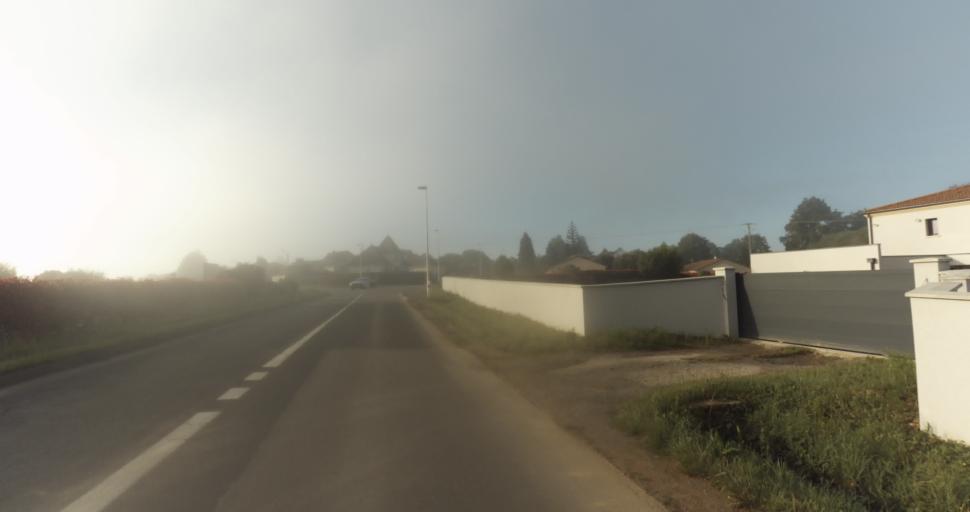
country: FR
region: Limousin
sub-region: Departement de la Haute-Vienne
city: Condat-sur-Vienne
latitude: 45.7876
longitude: 1.2865
